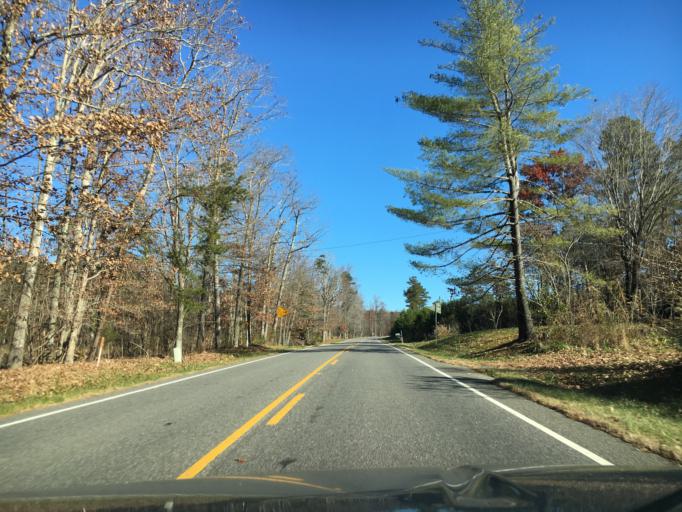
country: US
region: Virginia
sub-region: Appomattox County
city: Appomattox
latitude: 37.4520
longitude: -78.7148
